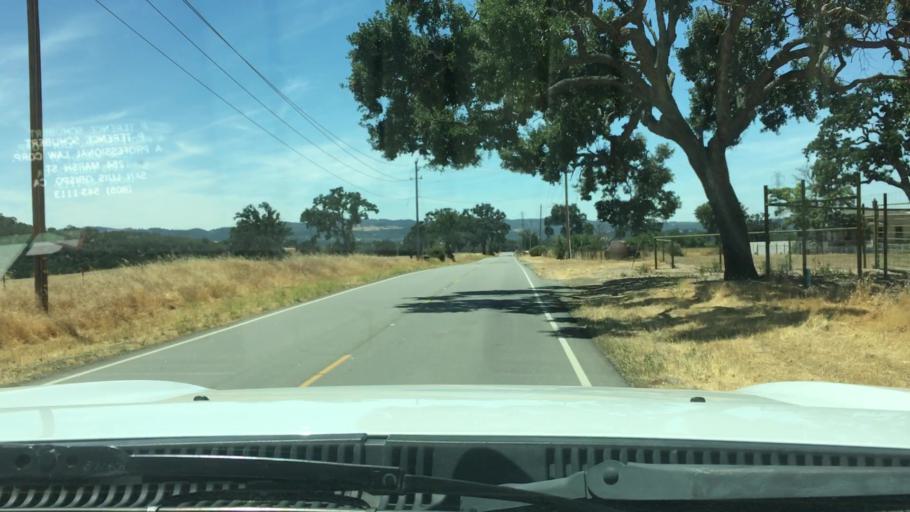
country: US
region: California
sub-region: San Luis Obispo County
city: Templeton
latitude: 35.5609
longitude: -120.6708
